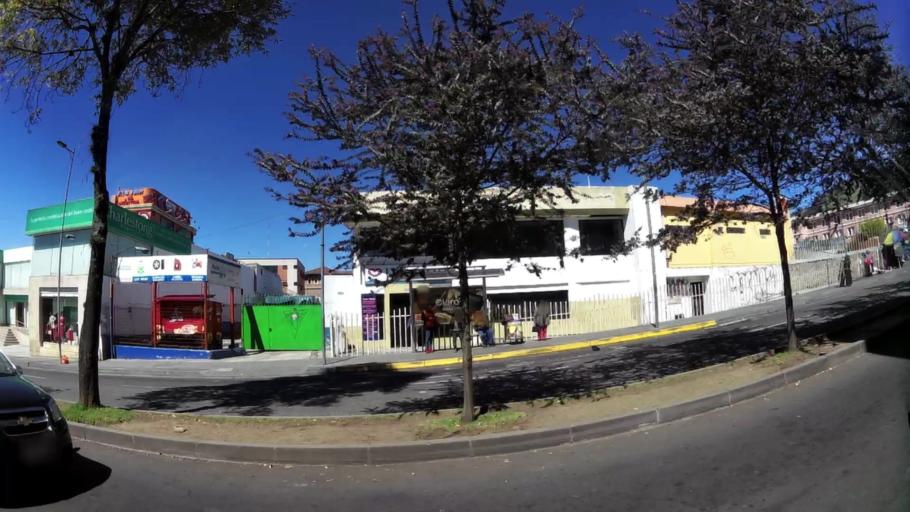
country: EC
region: Pichincha
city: Quito
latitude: -0.1964
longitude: -78.4992
